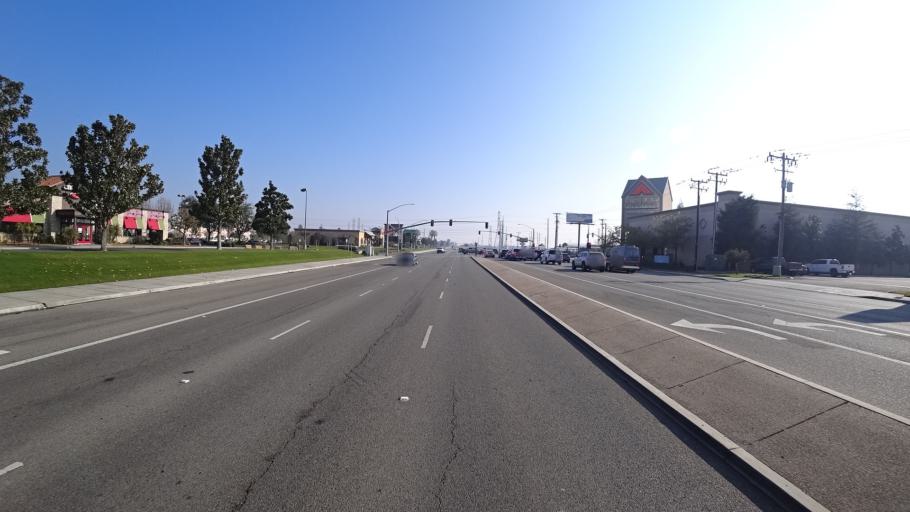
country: US
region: California
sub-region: Kern County
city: Greenacres
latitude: 35.3835
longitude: -119.1020
